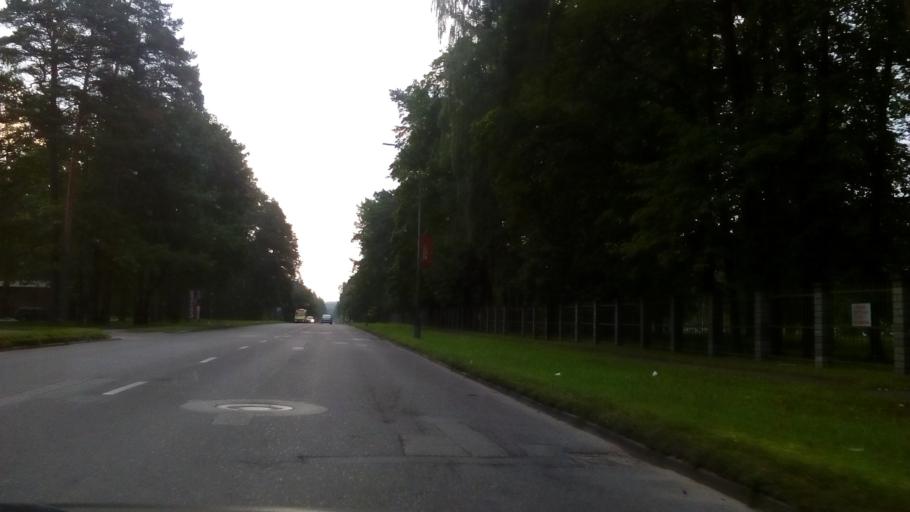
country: LT
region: Alytaus apskritis
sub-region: Alytus
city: Alytus
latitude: 54.3806
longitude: 24.0599
